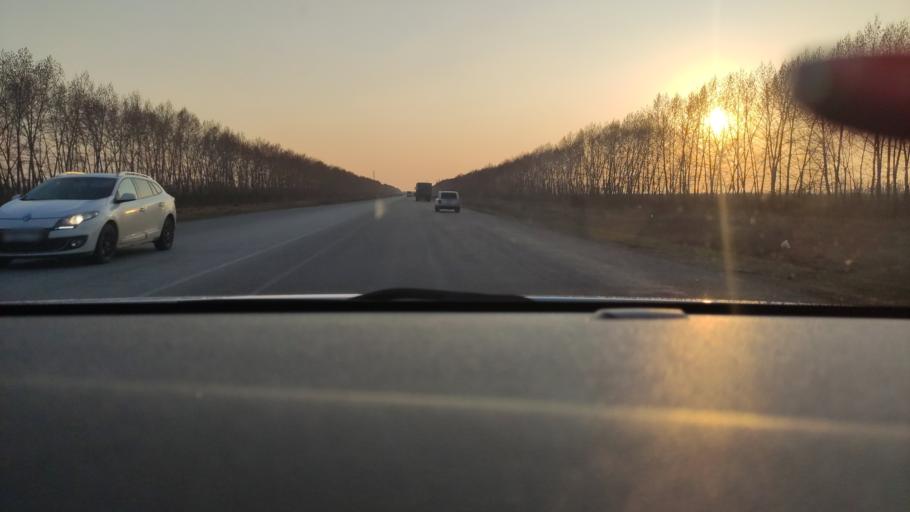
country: RU
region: Voronezj
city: Novovoronezh
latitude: 51.4210
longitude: 39.2909
